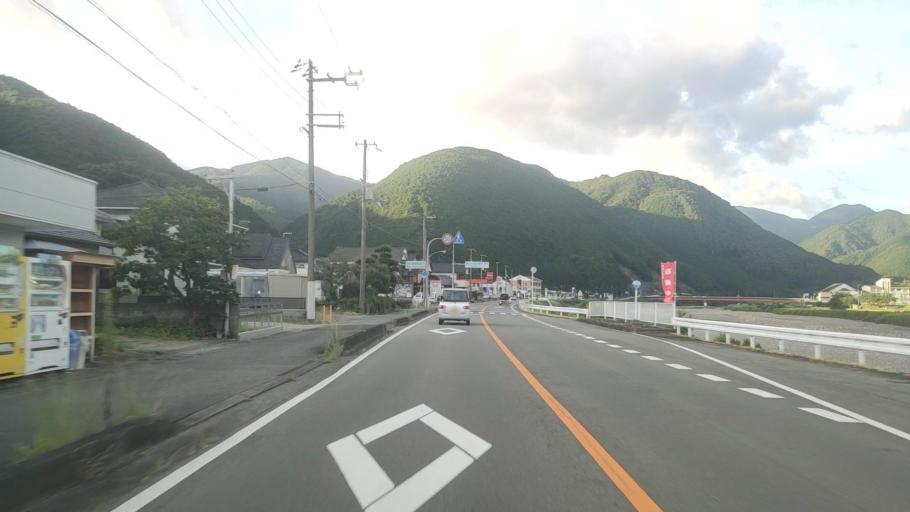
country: JP
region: Wakayama
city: Tanabe
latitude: 33.7267
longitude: 135.4827
